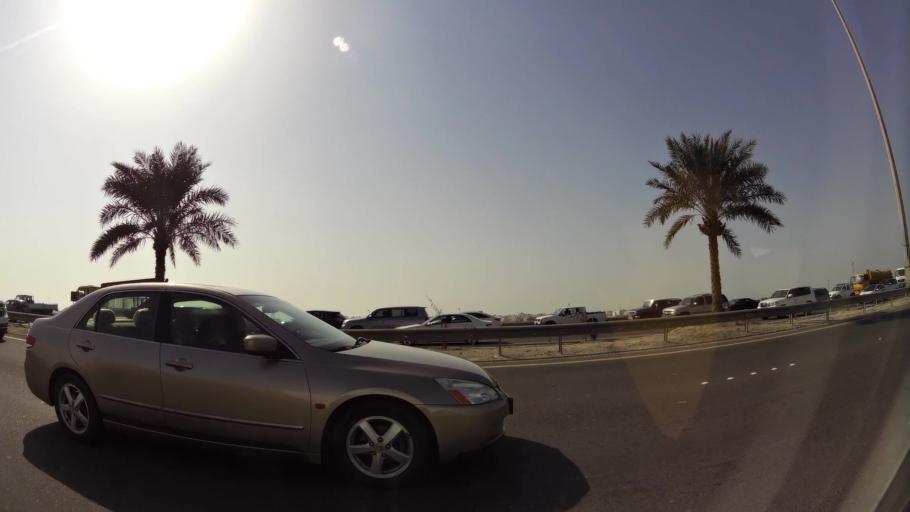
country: BH
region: Northern
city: Madinat `Isa
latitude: 26.1872
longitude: 50.5038
